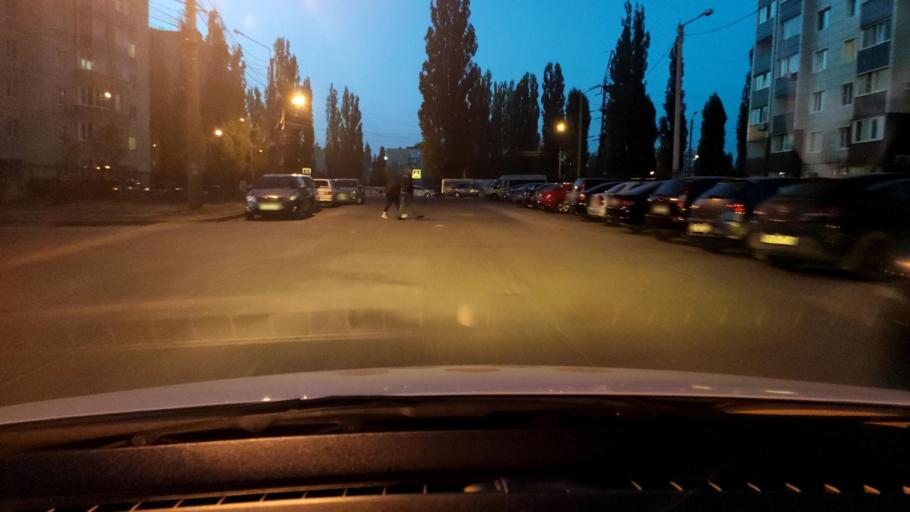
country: RU
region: Voronezj
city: Podgornoye
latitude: 51.6961
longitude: 39.1346
